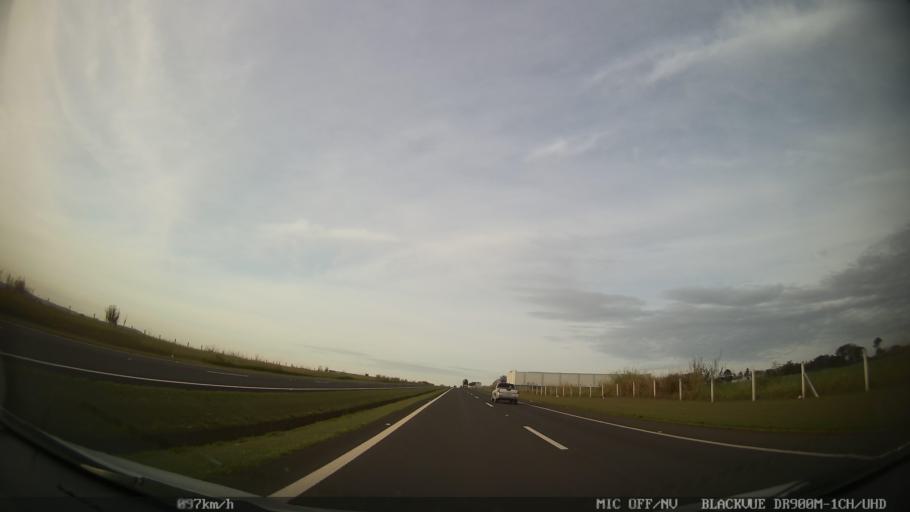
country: BR
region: Sao Paulo
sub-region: Iracemapolis
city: Iracemapolis
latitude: -22.6170
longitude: -47.4835
